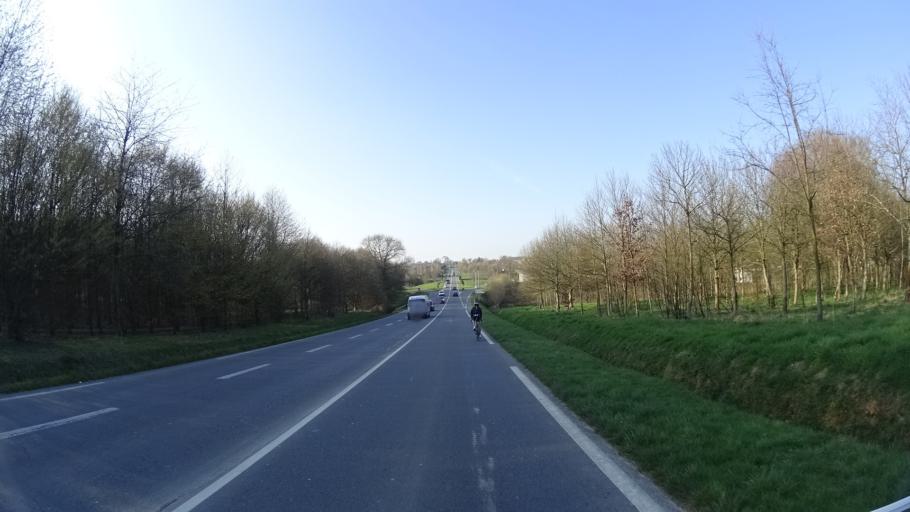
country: FR
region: Brittany
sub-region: Departement d'Ille-et-Vilaine
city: Melesse
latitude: 48.2104
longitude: -1.6993
